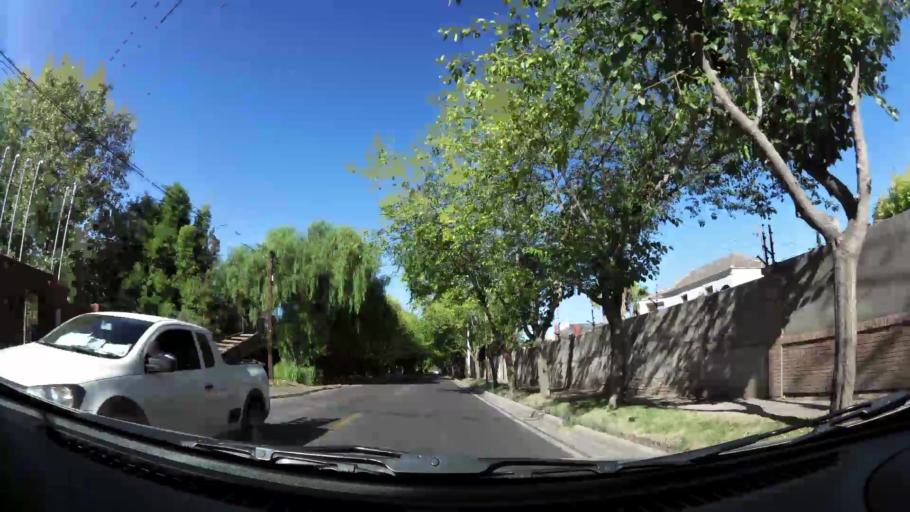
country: AR
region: Mendoza
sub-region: Departamento de Godoy Cruz
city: Godoy Cruz
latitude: -32.9150
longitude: -68.8092
